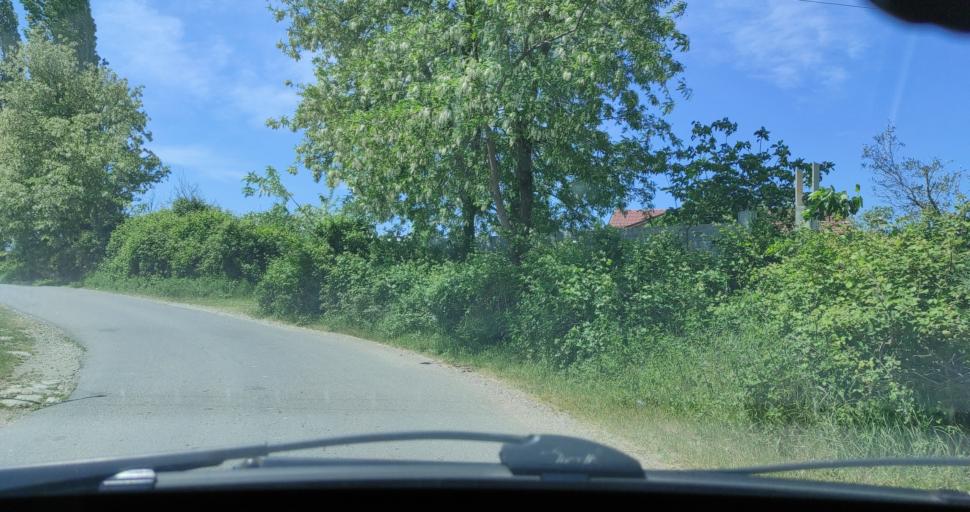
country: AL
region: Lezhe
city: Lezhe
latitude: 41.7565
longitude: 19.6116
